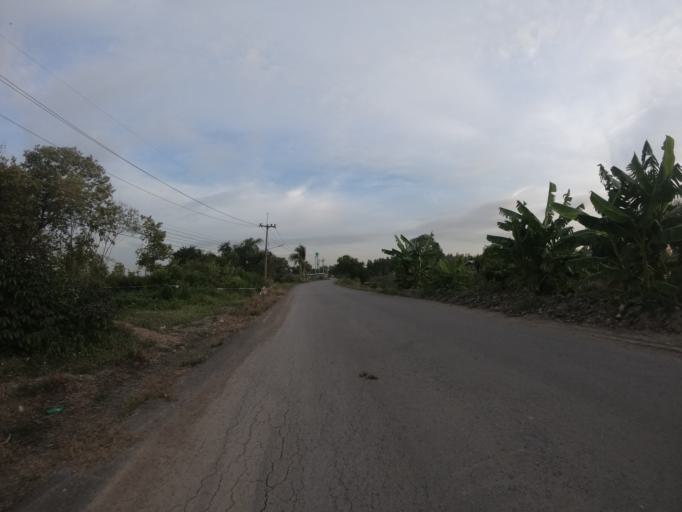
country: TH
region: Pathum Thani
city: Ban Lam Luk Ka
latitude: 14.0083
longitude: 100.7988
